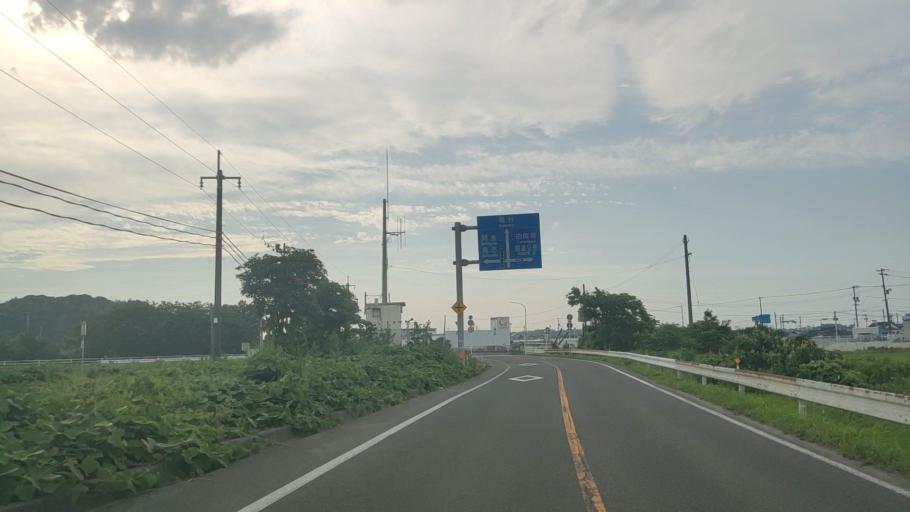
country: JP
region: Tottori
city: Kurayoshi
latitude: 35.4795
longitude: 133.8154
